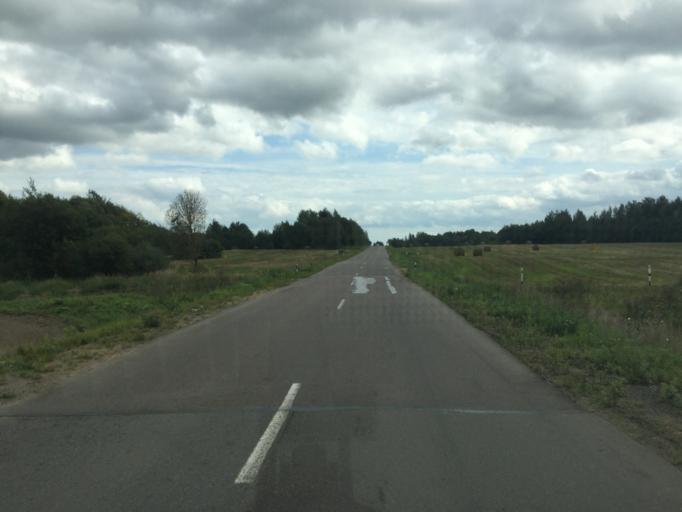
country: BY
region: Vitebsk
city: Vitebsk
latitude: 55.1321
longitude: 30.3102
